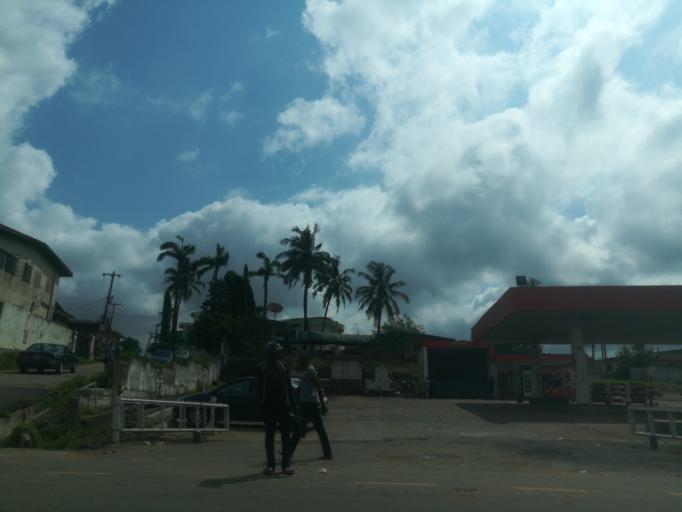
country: NG
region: Oyo
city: Ibadan
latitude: 7.3360
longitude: 3.8703
